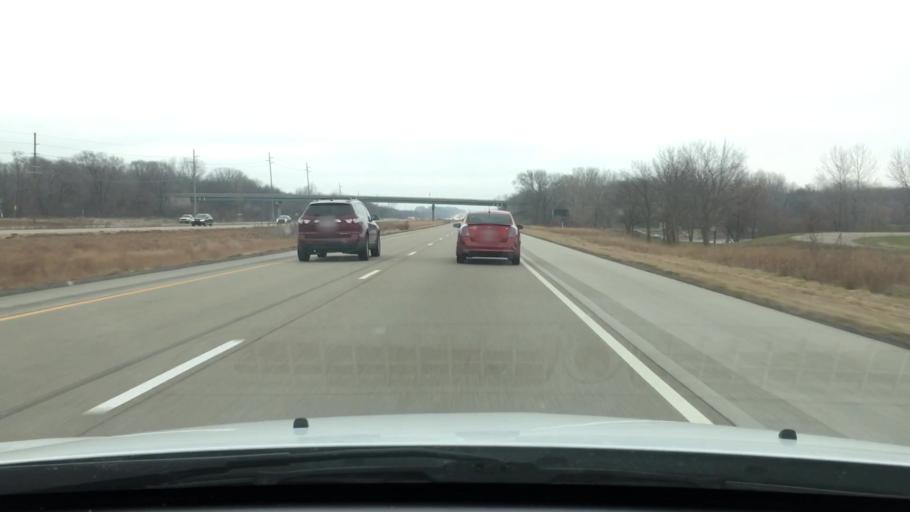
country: US
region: Illinois
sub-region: Logan County
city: Atlanta
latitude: 40.2178
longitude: -89.2810
